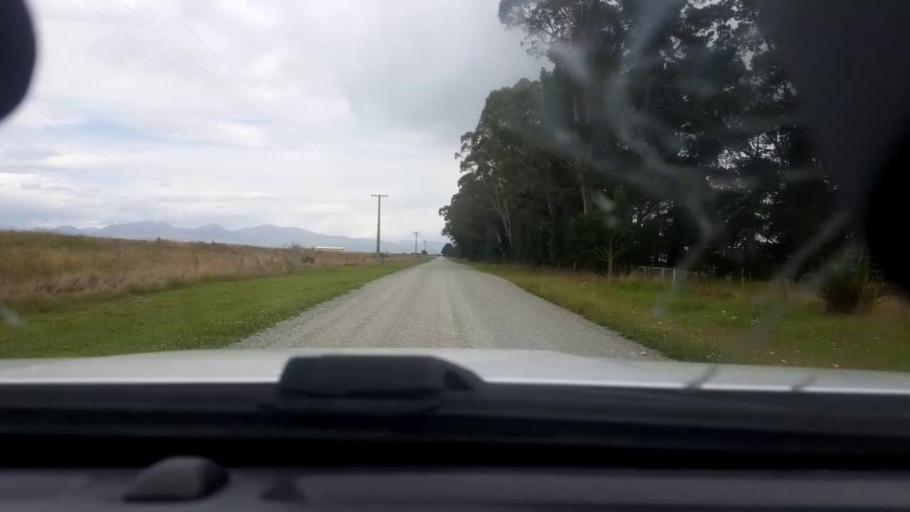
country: NZ
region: Canterbury
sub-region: Timaru District
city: Pleasant Point
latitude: -44.1513
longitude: 171.3949
